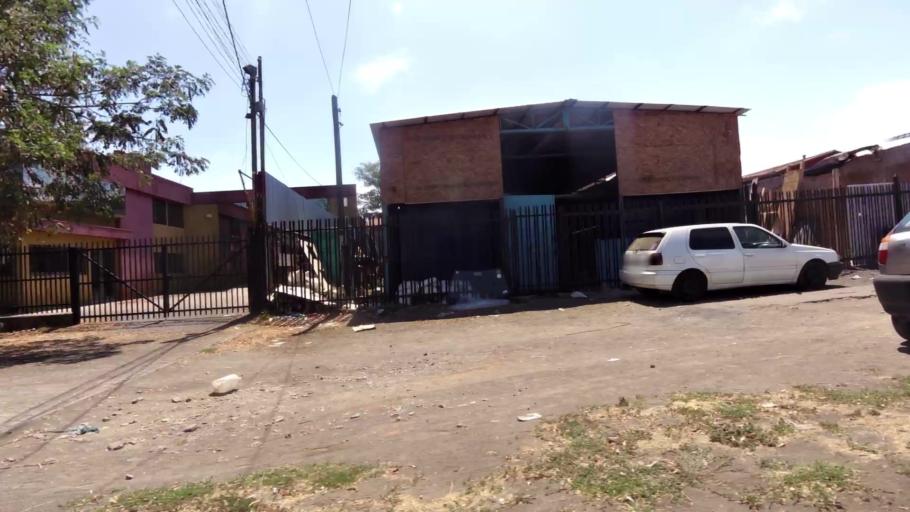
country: CL
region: Biobio
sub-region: Provincia de Concepcion
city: Concepcion
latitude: -36.8088
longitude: -73.0488
